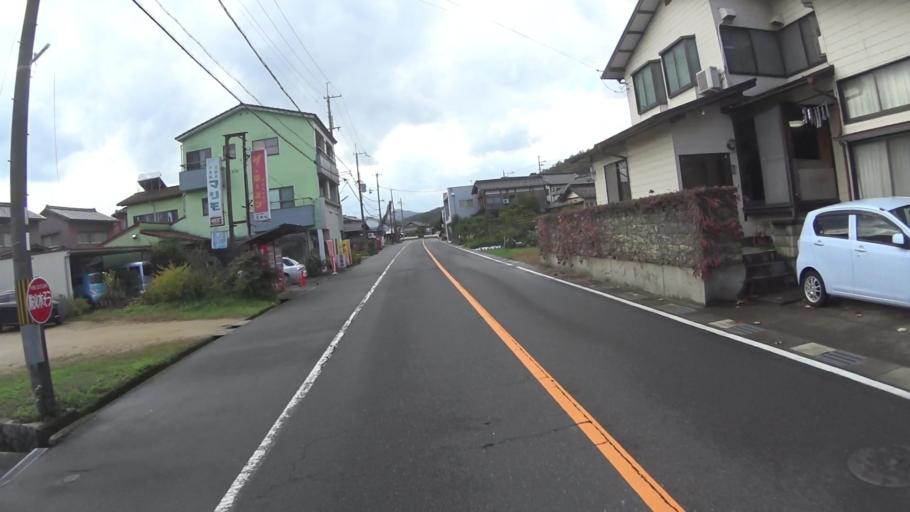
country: JP
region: Kyoto
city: Miyazu
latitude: 35.5428
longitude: 135.1240
